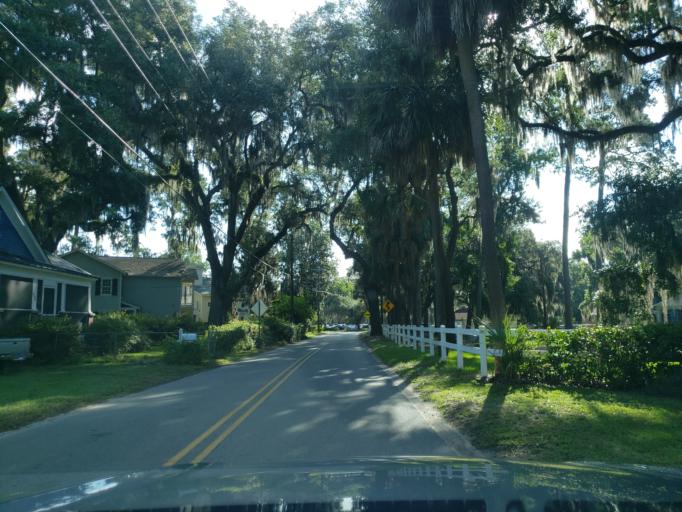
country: US
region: Georgia
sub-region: Chatham County
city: Isle of Hope
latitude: 31.9807
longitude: -81.0611
